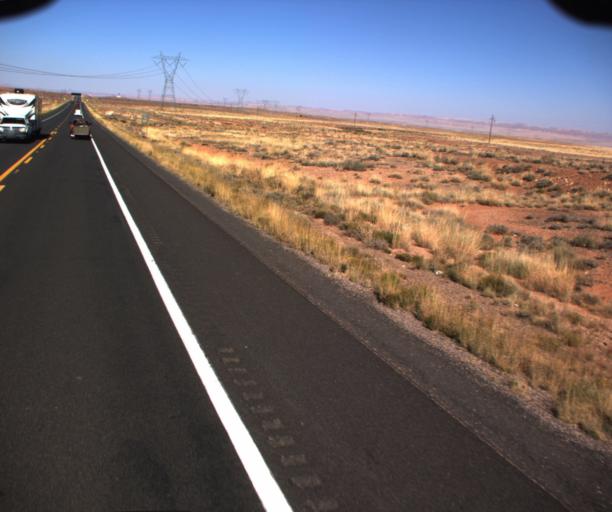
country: US
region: Arizona
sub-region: Coconino County
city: Tuba City
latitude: 35.8156
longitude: -111.4421
